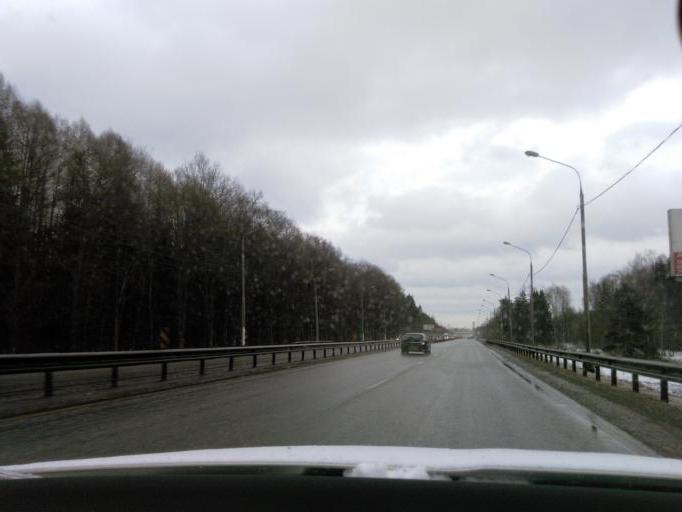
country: RU
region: Moskovskaya
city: Mendeleyevo
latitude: 56.0077
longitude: 37.2242
